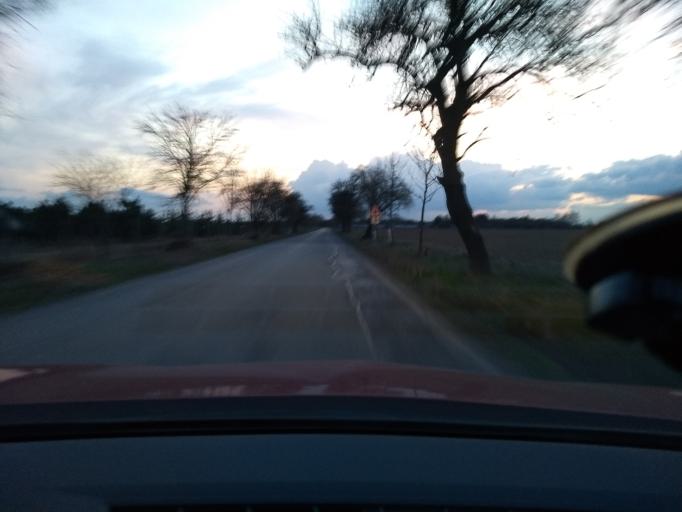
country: CZ
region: Central Bohemia
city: Jenec
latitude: 50.0688
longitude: 14.2160
